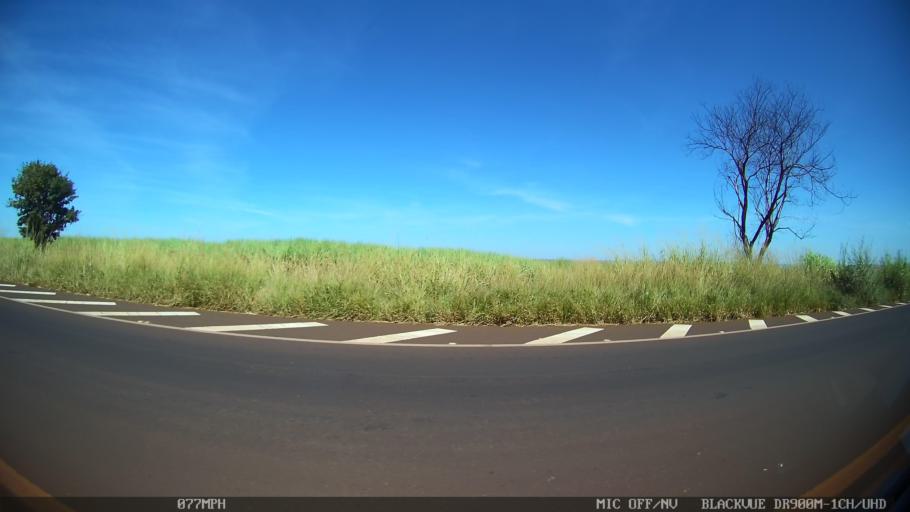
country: BR
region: Sao Paulo
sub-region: Sao Joaquim Da Barra
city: Sao Joaquim da Barra
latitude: -20.5437
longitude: -47.7896
